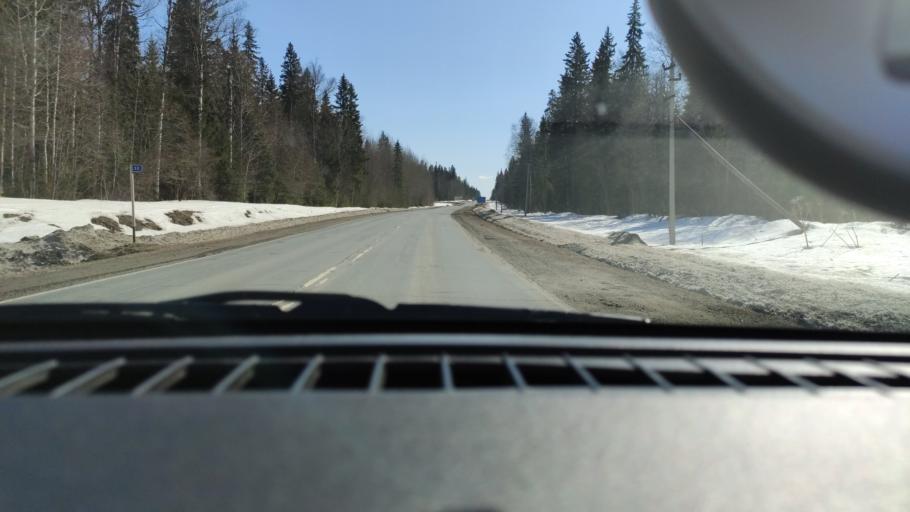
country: RU
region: Perm
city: Perm
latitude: 58.2010
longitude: 56.2050
